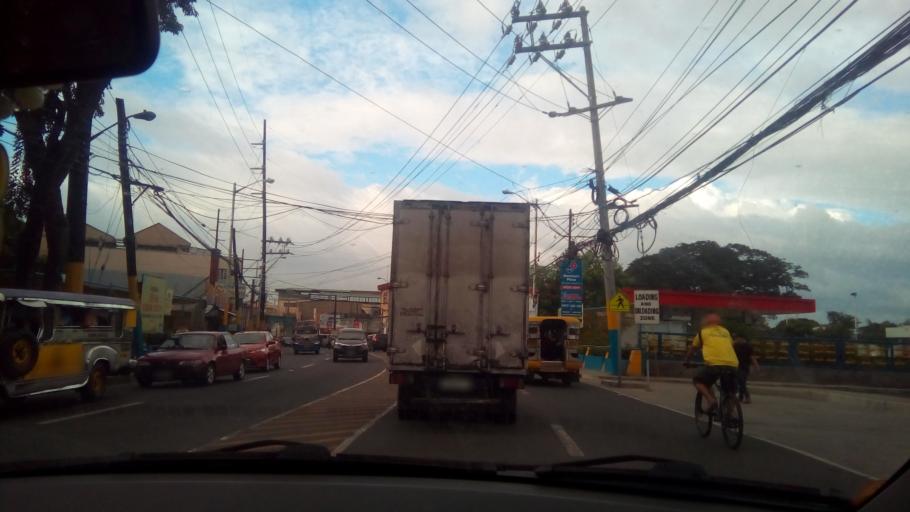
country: PH
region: Calabarzon
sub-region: Province of Laguna
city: San Pedro
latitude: 14.3878
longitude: 121.0456
